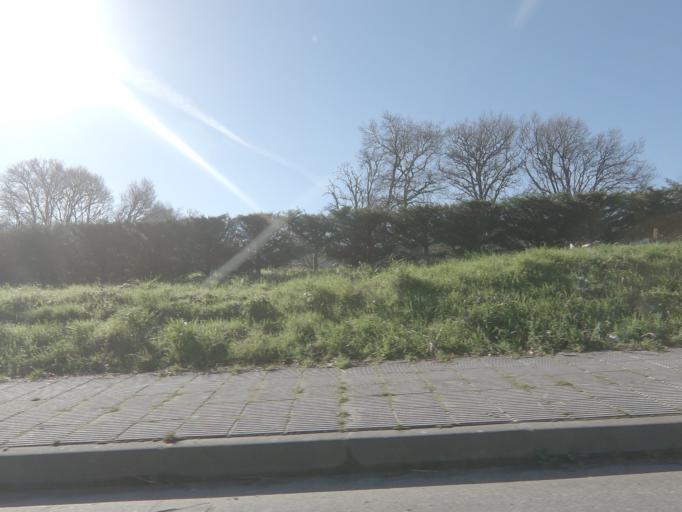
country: ES
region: Galicia
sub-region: Provincia de Pontevedra
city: Silleda
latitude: 42.6950
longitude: -8.2355
